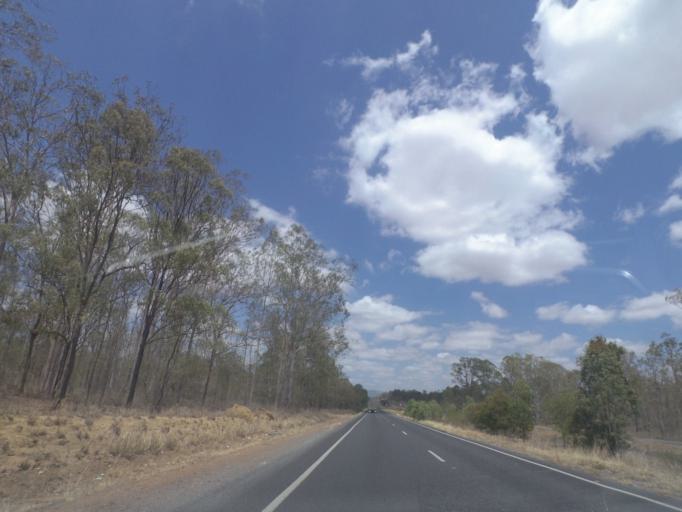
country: AU
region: Queensland
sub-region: Lockyer Valley
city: Gatton
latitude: -27.5518
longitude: 152.1481
